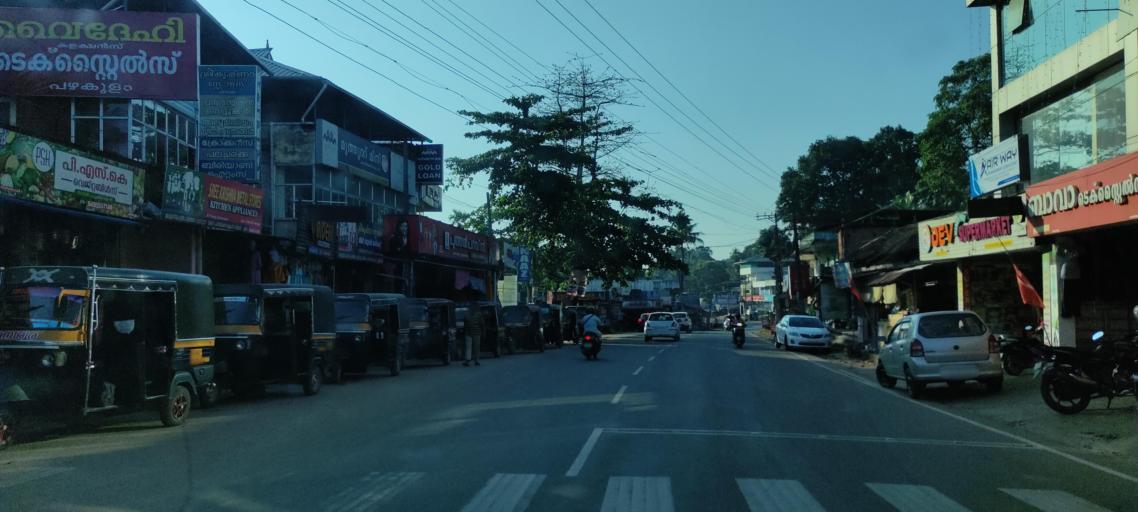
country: IN
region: Kerala
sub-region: Pattanamtitta
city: Adur
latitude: 9.1653
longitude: 76.6845
